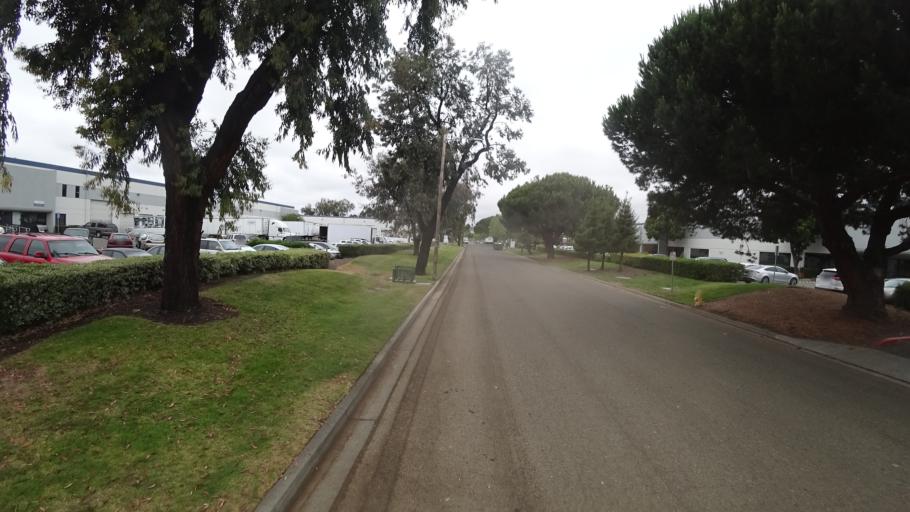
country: US
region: California
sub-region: Alameda County
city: Union City
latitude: 37.6150
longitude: -122.0573
